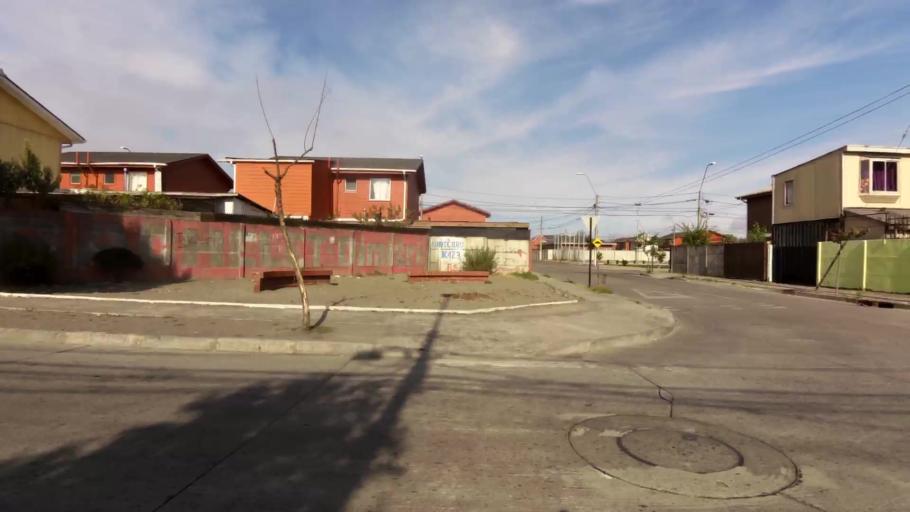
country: CL
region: Biobio
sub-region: Provincia de Concepcion
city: Talcahuano
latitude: -36.7951
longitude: -73.1147
